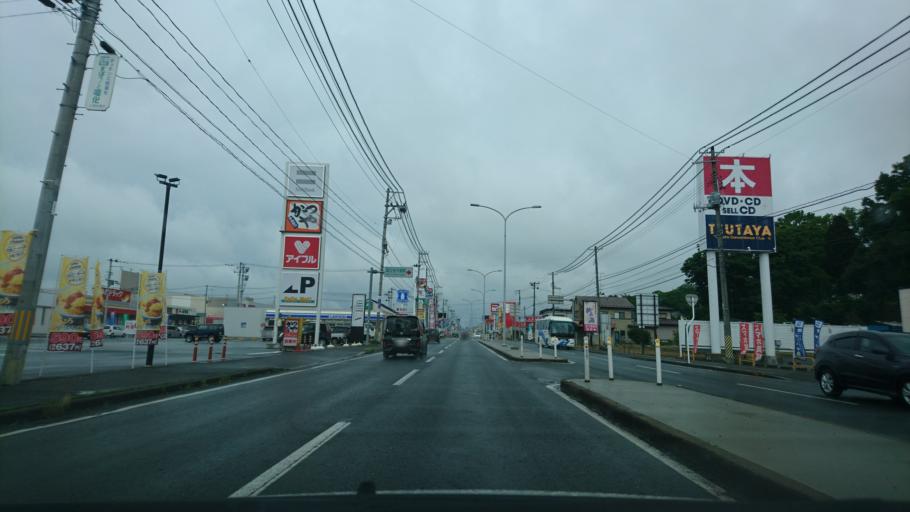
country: JP
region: Iwate
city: Ichinoseki
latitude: 38.9376
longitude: 141.1157
